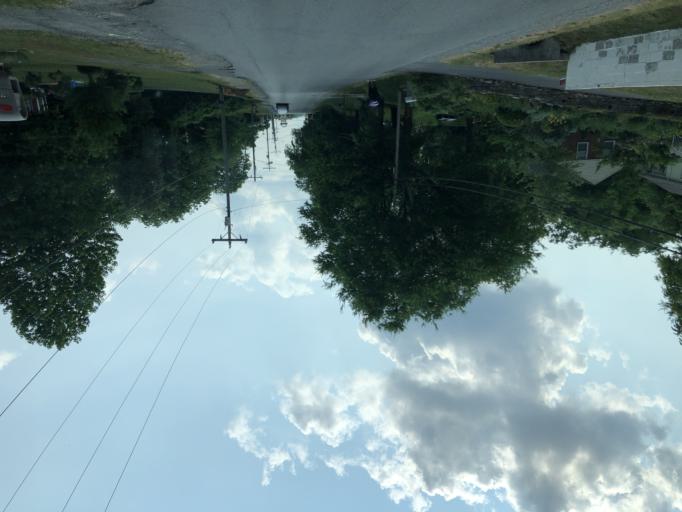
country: US
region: Tennessee
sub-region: Davidson County
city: Goodlettsville
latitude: 36.2478
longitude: -86.7168
